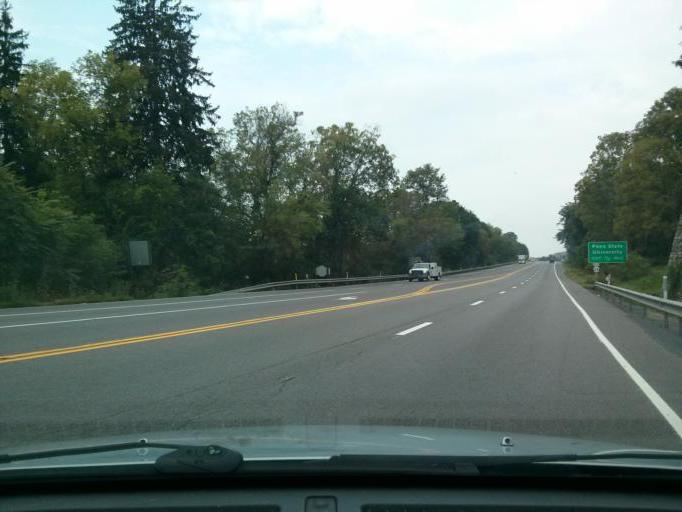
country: US
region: Pennsylvania
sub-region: Centre County
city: State College
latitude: 40.8053
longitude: -77.8430
